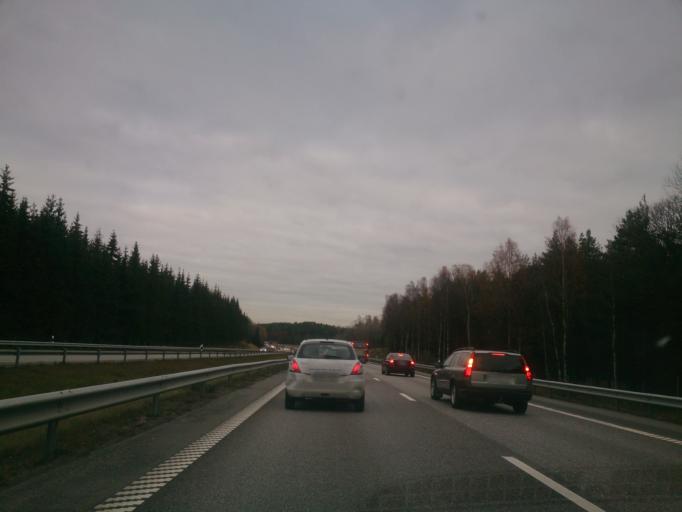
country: SE
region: Stockholm
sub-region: Sodertalje Kommun
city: Pershagen
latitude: 59.1004
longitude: 17.6076
